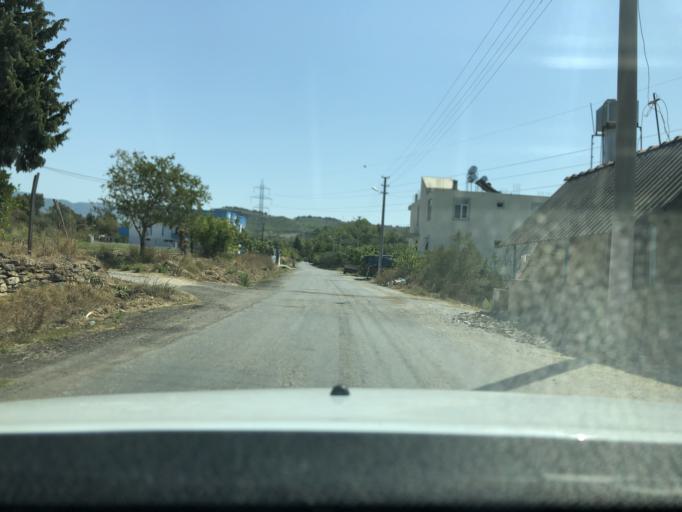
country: TR
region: Antalya
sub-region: Manavgat
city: Manavgat
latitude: 36.8216
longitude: 31.5023
